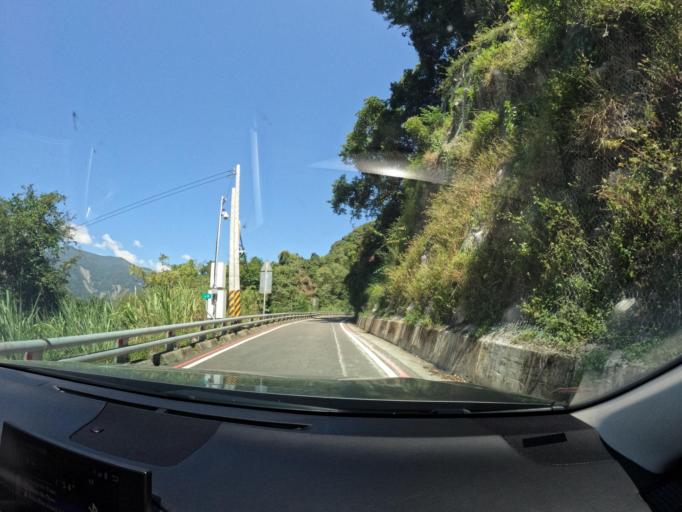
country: TW
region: Taiwan
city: Yujing
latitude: 23.2596
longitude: 120.8508
